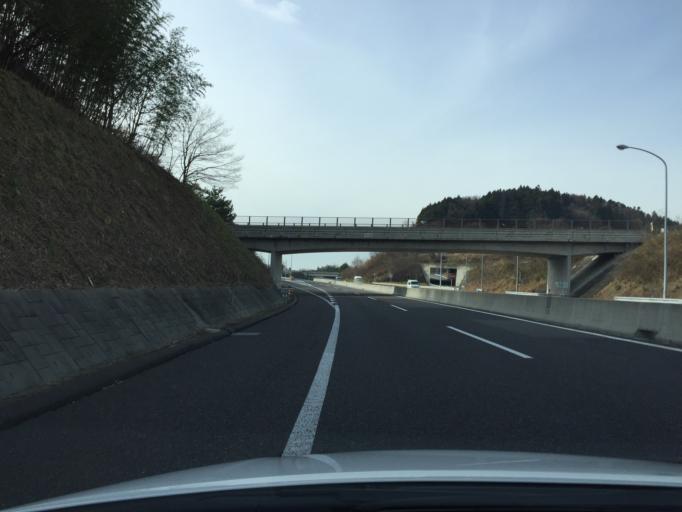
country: JP
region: Fukushima
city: Miharu
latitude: 37.4290
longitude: 140.4874
